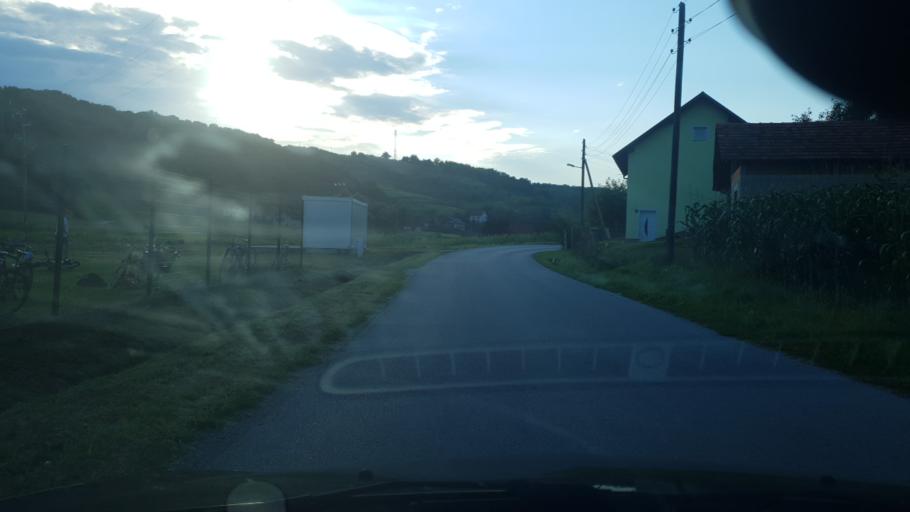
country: HR
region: Krapinsko-Zagorska
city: Zabok
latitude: 46.0380
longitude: 15.8929
